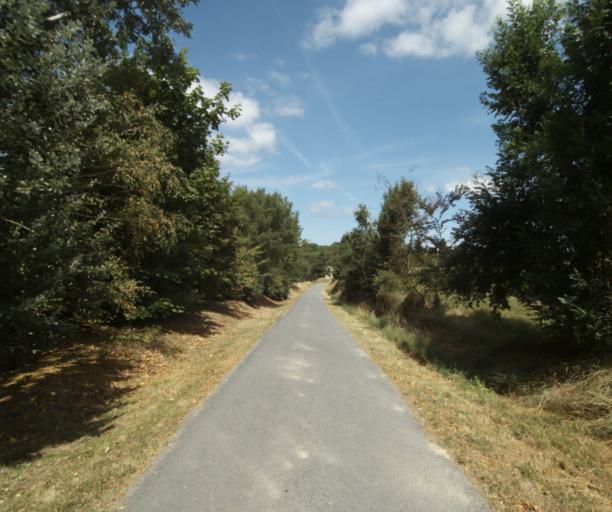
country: FR
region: Midi-Pyrenees
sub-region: Departement du Tarn
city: Dourgne
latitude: 43.5007
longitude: 2.0953
